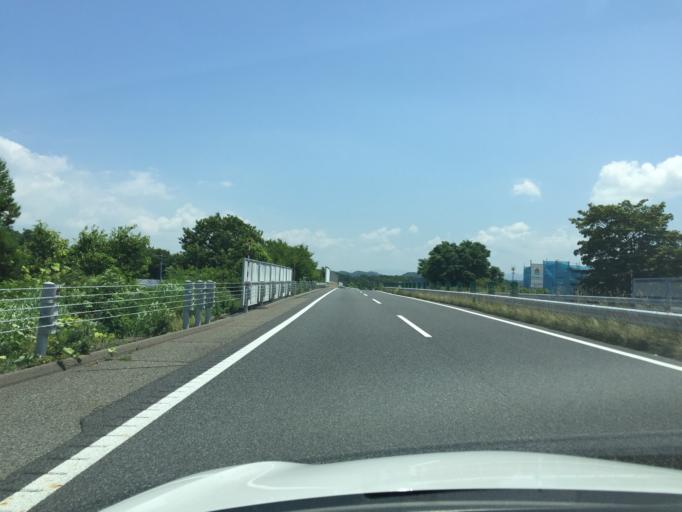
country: JP
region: Fukushima
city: Koriyama
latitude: 37.4526
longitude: 140.4051
